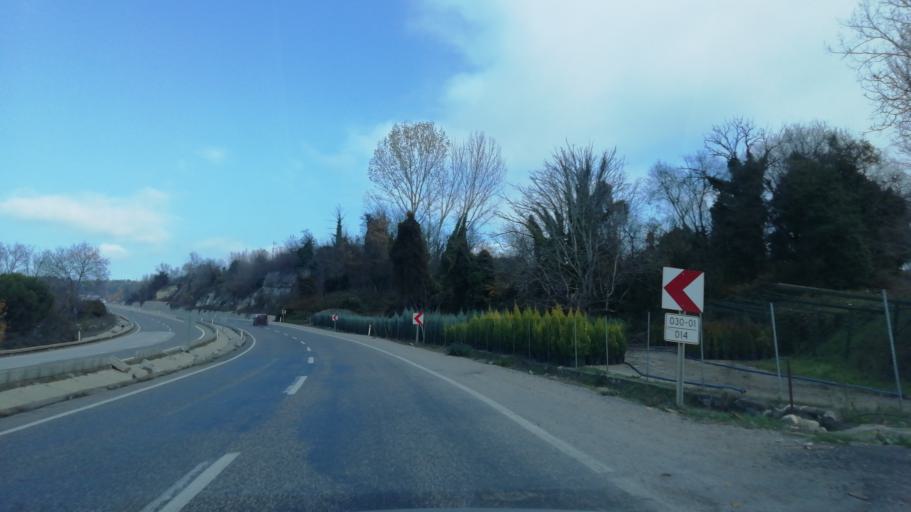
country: TR
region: Karabuk
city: Safranbolu
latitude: 41.2173
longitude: 32.7660
